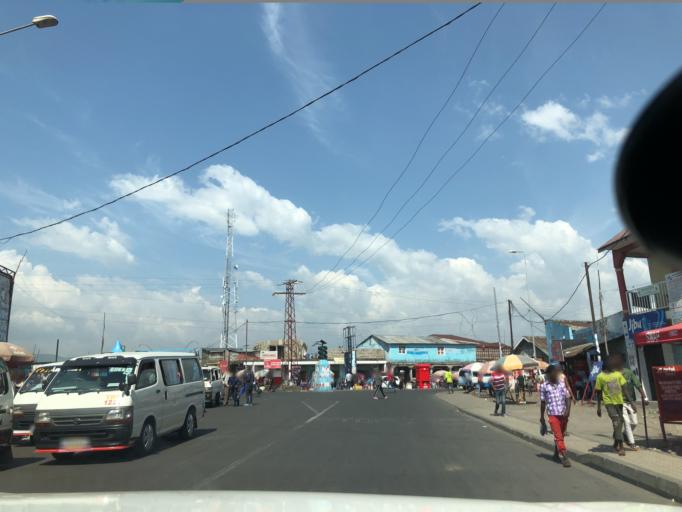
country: CD
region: Nord Kivu
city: Goma
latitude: -1.6566
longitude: 29.1969
